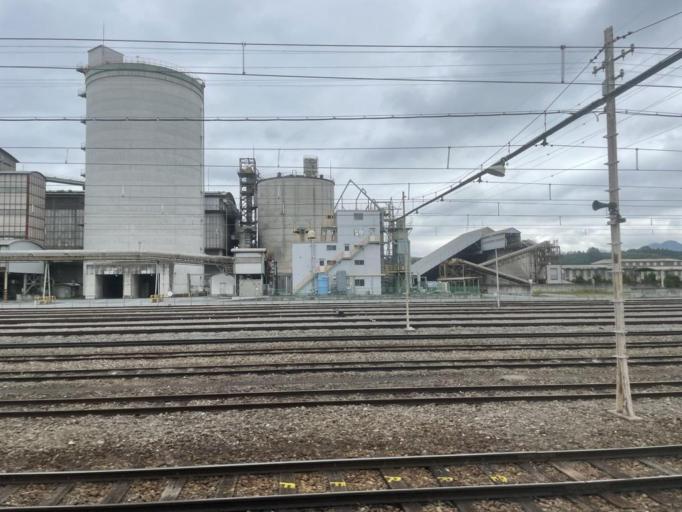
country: JP
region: Saitama
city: Chichibu
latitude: 36.0289
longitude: 139.0970
